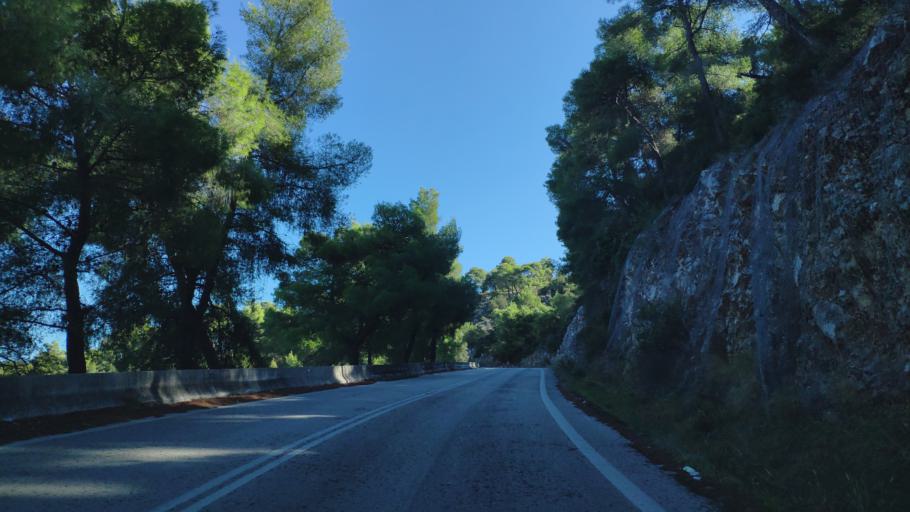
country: GR
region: Peloponnese
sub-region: Nomos Korinthias
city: Sofikon
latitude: 37.8280
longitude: 23.0745
